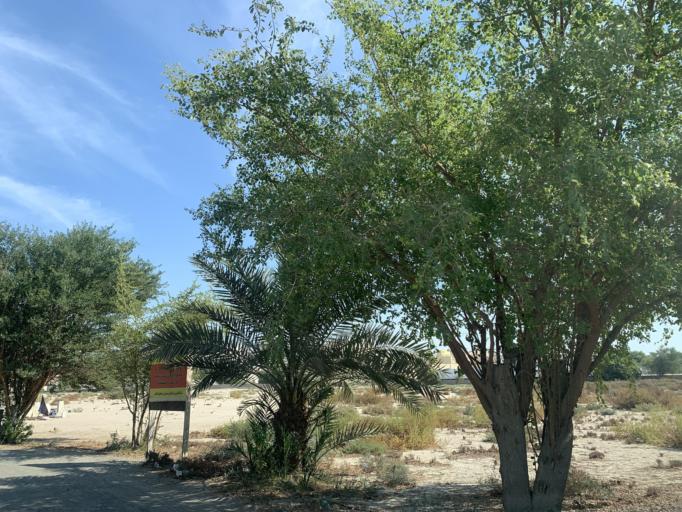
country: BH
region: Central Governorate
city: Madinat Hamad
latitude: 26.1139
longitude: 50.4847
